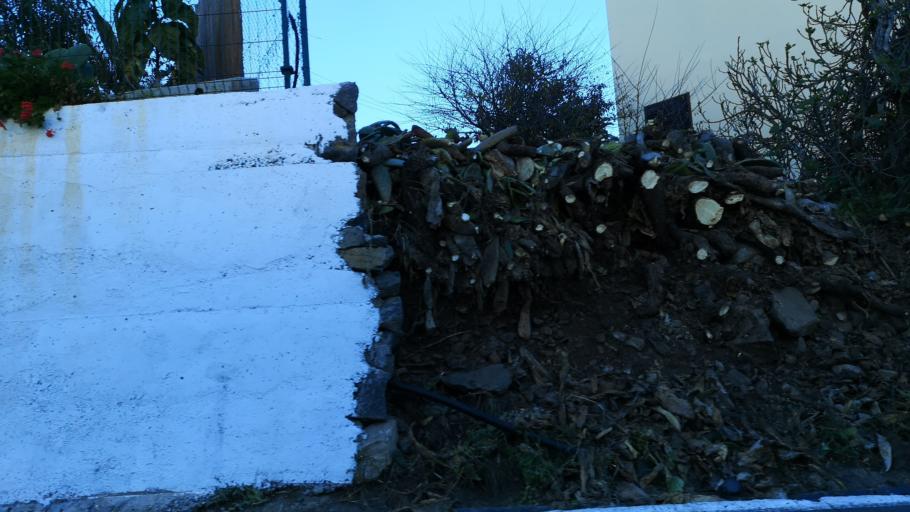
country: ES
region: Canary Islands
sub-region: Provincia de Santa Cruz de Tenerife
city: Alajero
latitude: 28.0575
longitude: -17.2341
